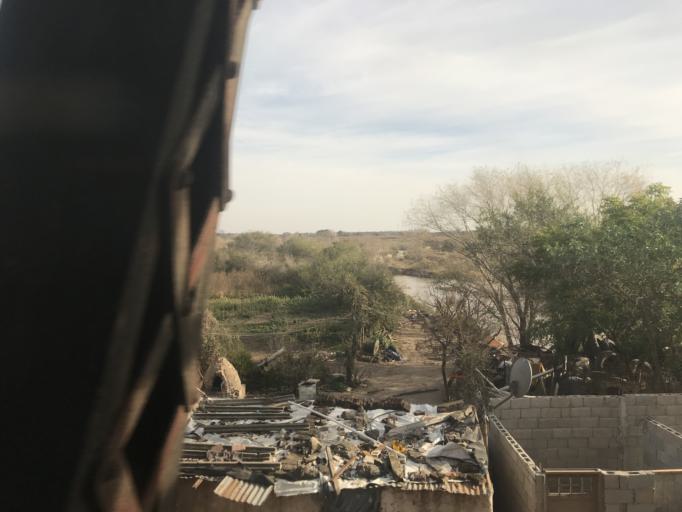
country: AR
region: Cordoba
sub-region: Departamento de Rio Segundo
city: Rio Segundo
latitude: -31.6634
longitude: -63.9019
